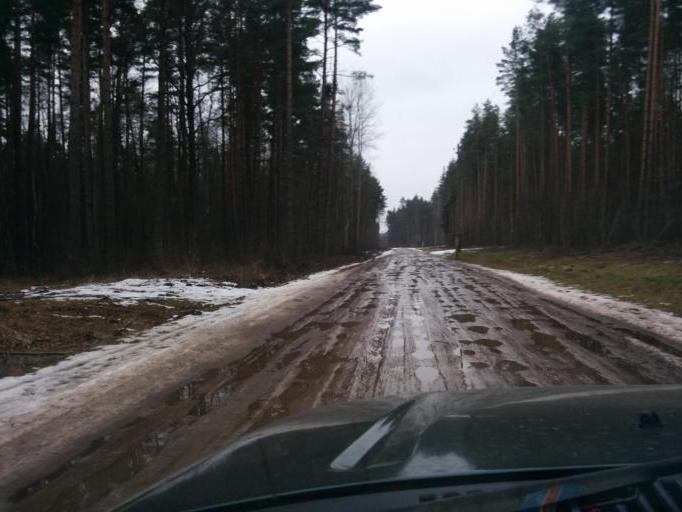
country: LV
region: Ozolnieku
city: Ozolnieki
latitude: 56.6776
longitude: 23.7597
